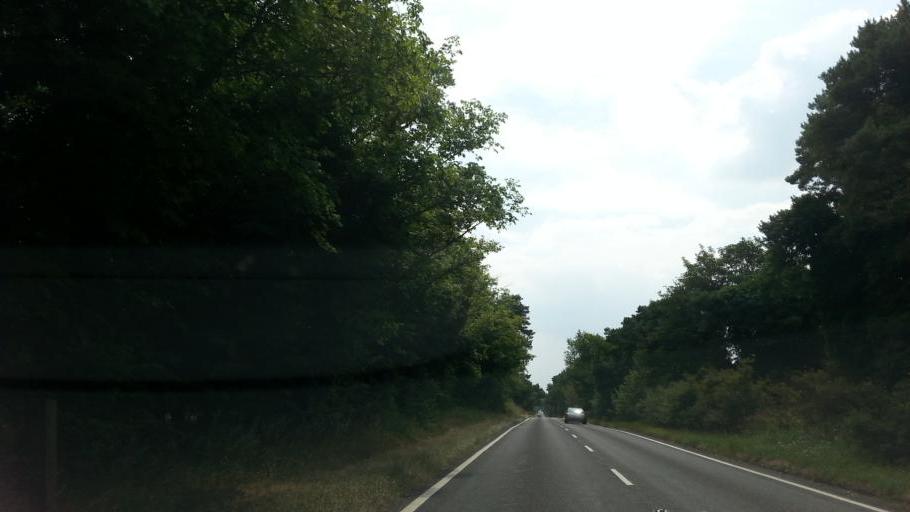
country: GB
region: England
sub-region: Suffolk
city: Lakenheath
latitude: 52.3624
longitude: 0.5394
